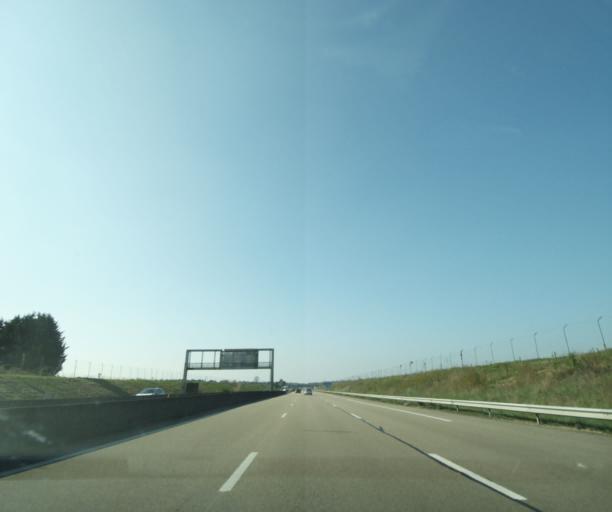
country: FR
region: Ile-de-France
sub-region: Departement de Seine-et-Marne
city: Acheres-la-Foret
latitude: 48.3562
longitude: 2.5814
